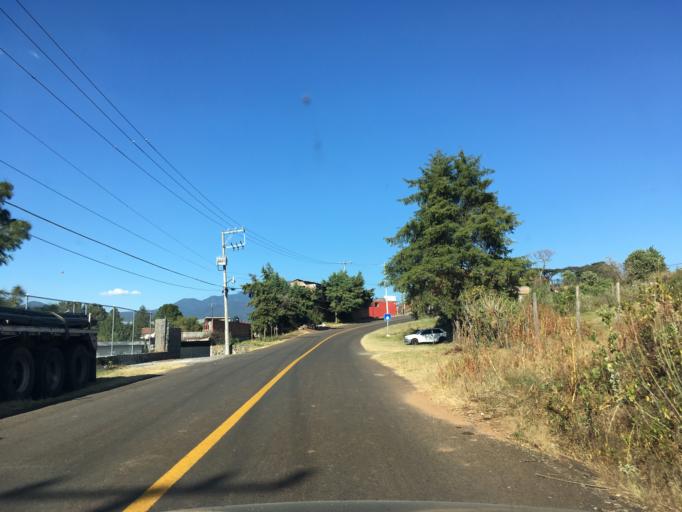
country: MX
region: Michoacan
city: Tzintzuntzan
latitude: 19.6242
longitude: -101.5761
